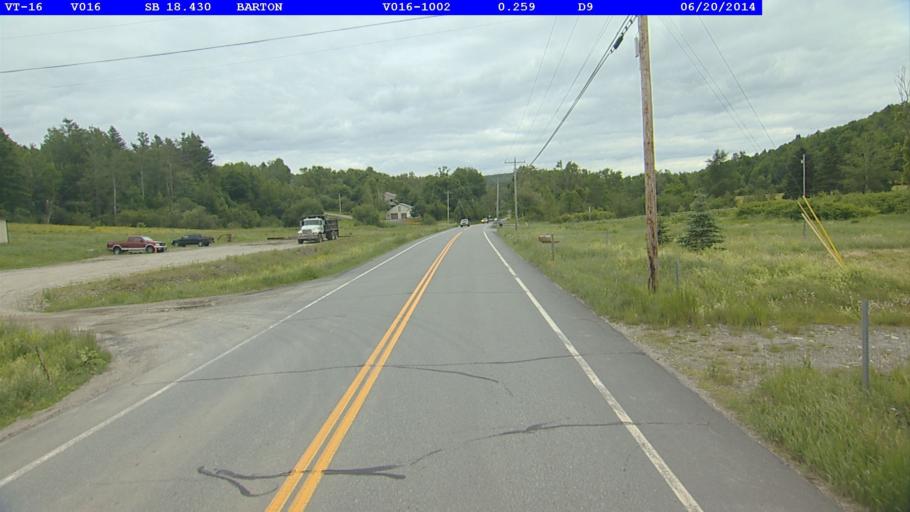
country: US
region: Vermont
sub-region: Orleans County
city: Newport
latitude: 44.7210
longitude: -72.1852
